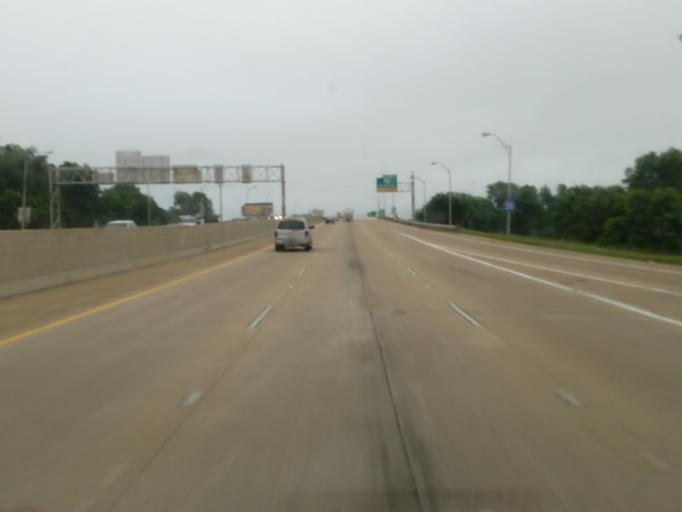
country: US
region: Louisiana
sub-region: Bossier Parish
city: Bossier City
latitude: 32.5138
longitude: -93.7246
